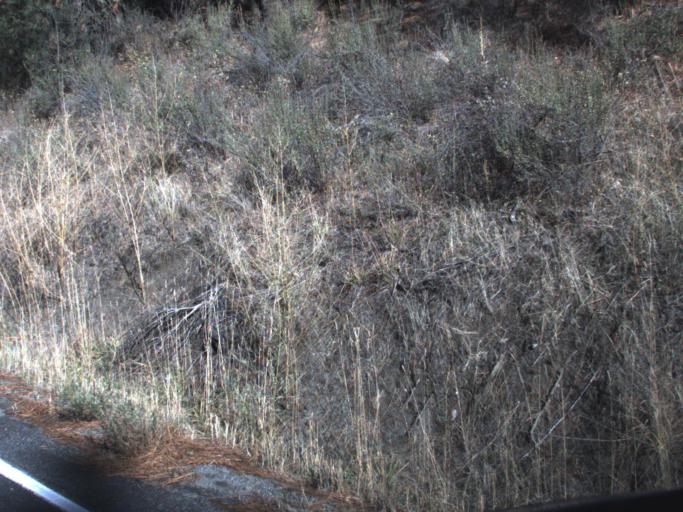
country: US
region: Washington
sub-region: Stevens County
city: Kettle Falls
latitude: 48.1943
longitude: -118.1710
